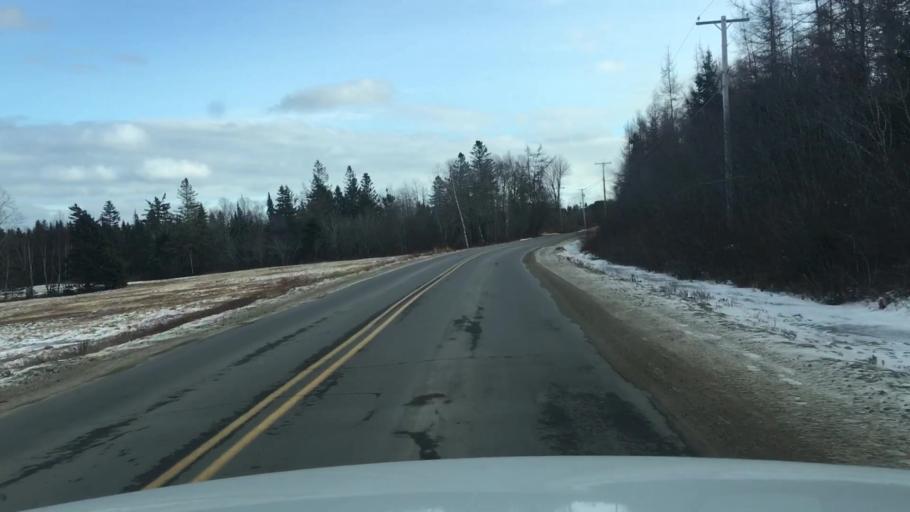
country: US
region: Maine
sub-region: Washington County
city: Jonesport
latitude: 44.6154
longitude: -67.6050
